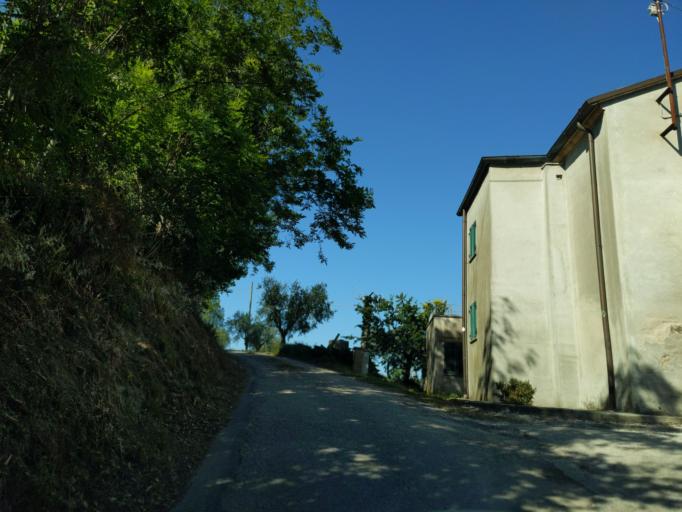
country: IT
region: The Marches
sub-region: Provincia di Pesaro e Urbino
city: Cuccurano
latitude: 43.7999
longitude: 12.9621
